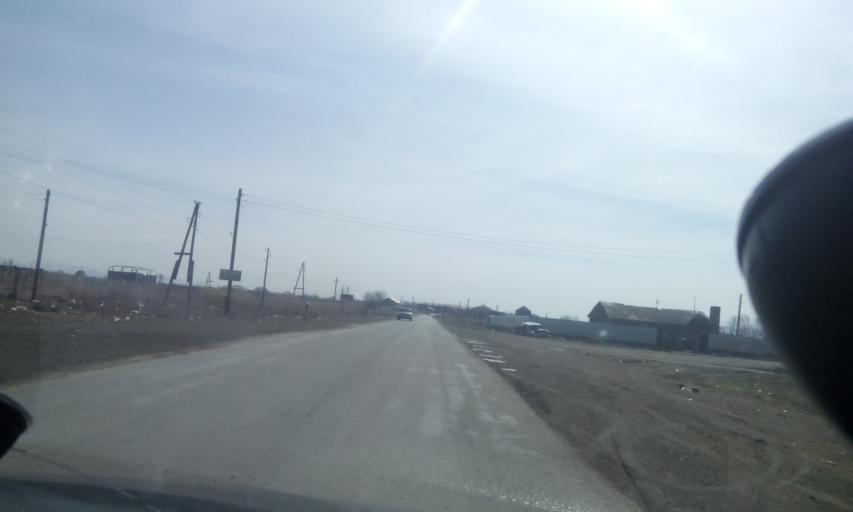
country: AM
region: Armavir
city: Tandzut
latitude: 40.0687
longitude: 44.0804
